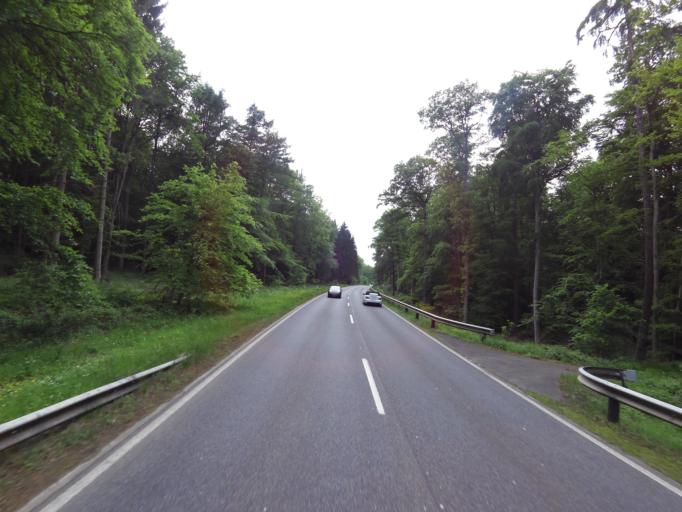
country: DE
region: Rheinland-Pfalz
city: Waldesch
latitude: 50.2929
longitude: 7.5630
